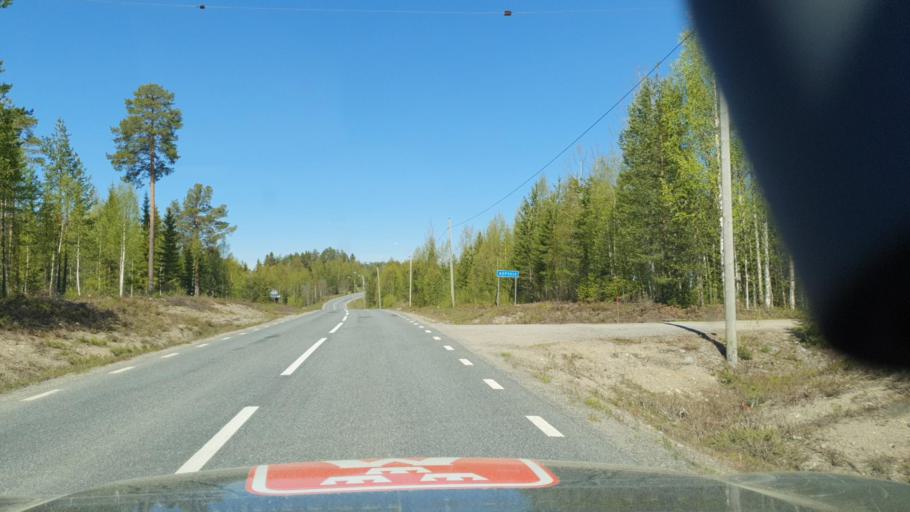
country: SE
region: Vaesternorrland
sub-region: OErnskoeldsviks Kommun
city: Bredbyn
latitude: 63.8456
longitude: 18.4725
